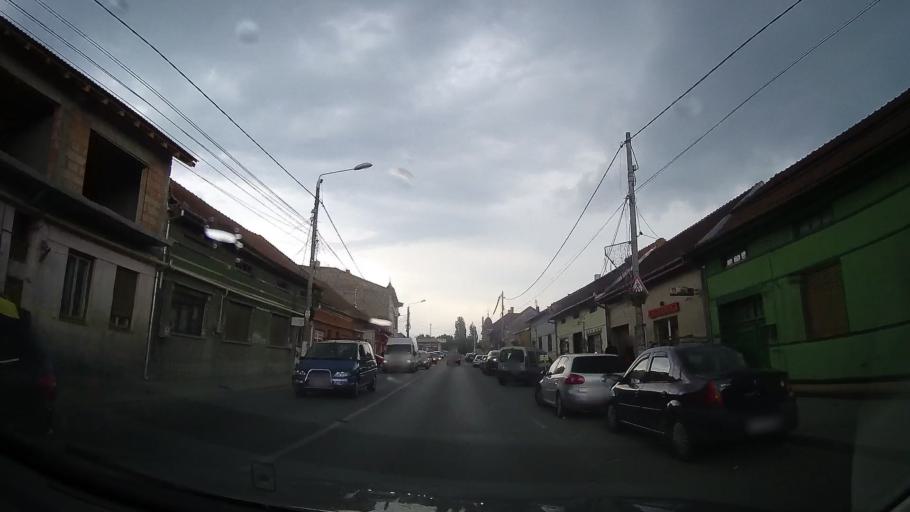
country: RO
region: Caras-Severin
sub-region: Municipiul Caransebes
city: Caransebes
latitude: 45.4093
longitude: 22.2203
